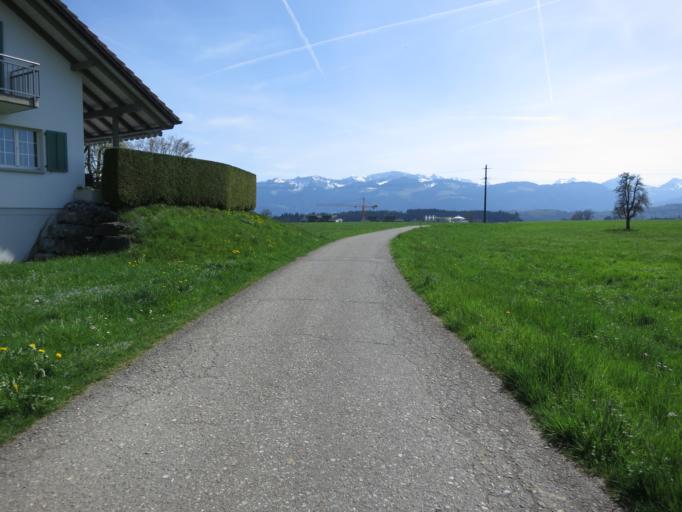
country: CH
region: Saint Gallen
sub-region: Wahlkreis See-Gaster
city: Schmerikon
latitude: 47.2481
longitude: 8.9466
